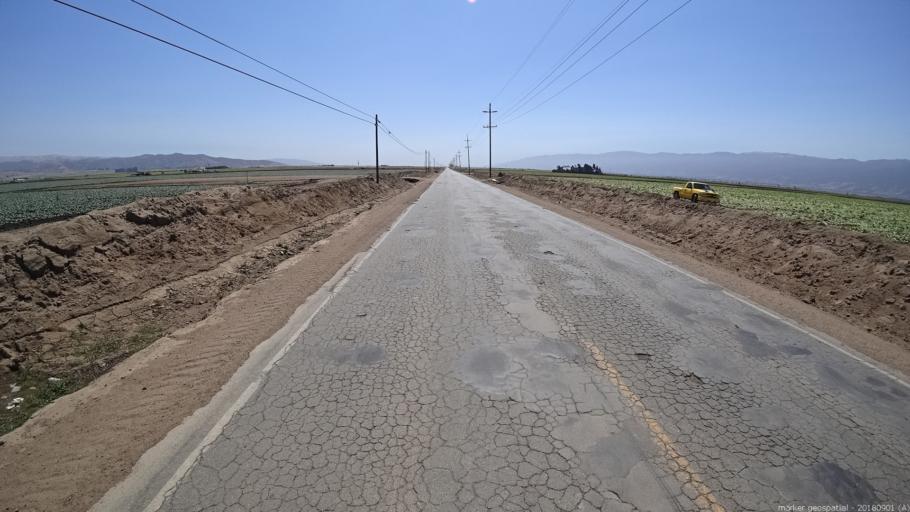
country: US
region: California
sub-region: Monterey County
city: Chualar
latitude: 36.6058
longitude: -121.5143
